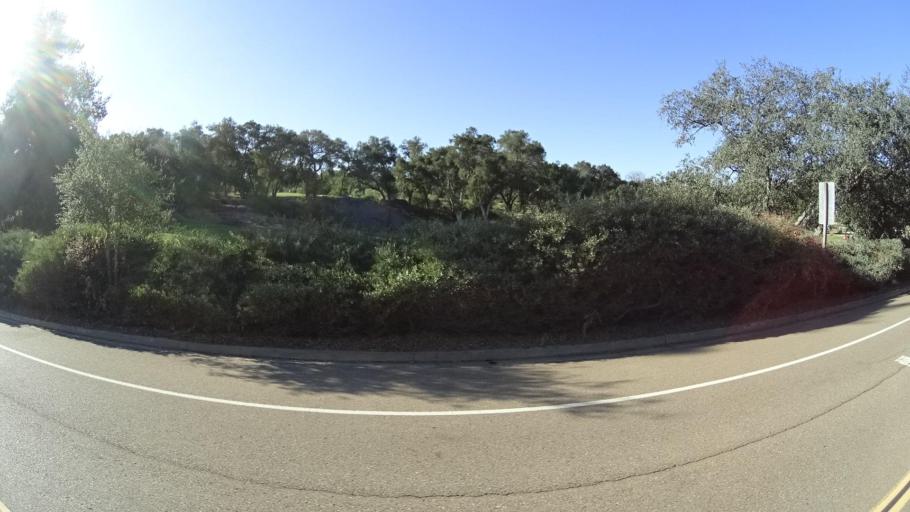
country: US
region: California
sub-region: San Diego County
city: Hidden Meadows
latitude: 33.2155
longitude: -117.1072
